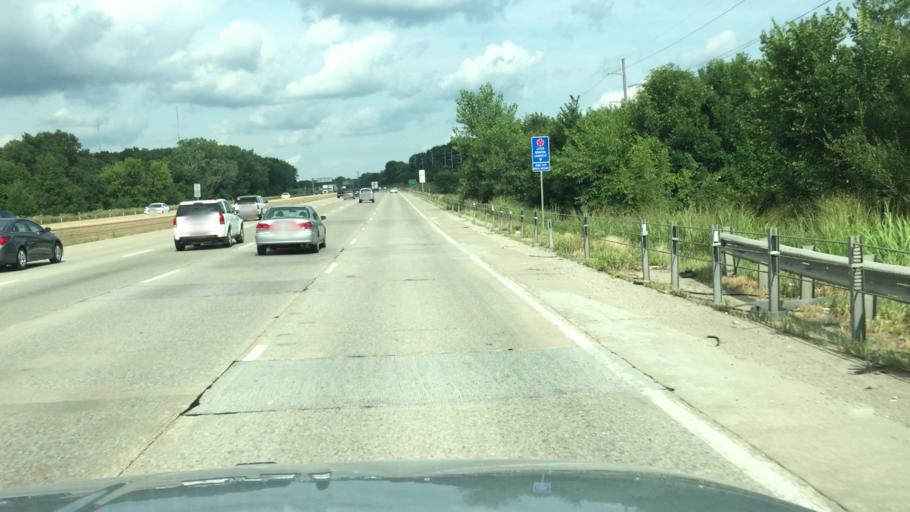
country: US
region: Iowa
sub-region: Johnson County
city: Coralville
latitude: 41.6851
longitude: -91.5554
